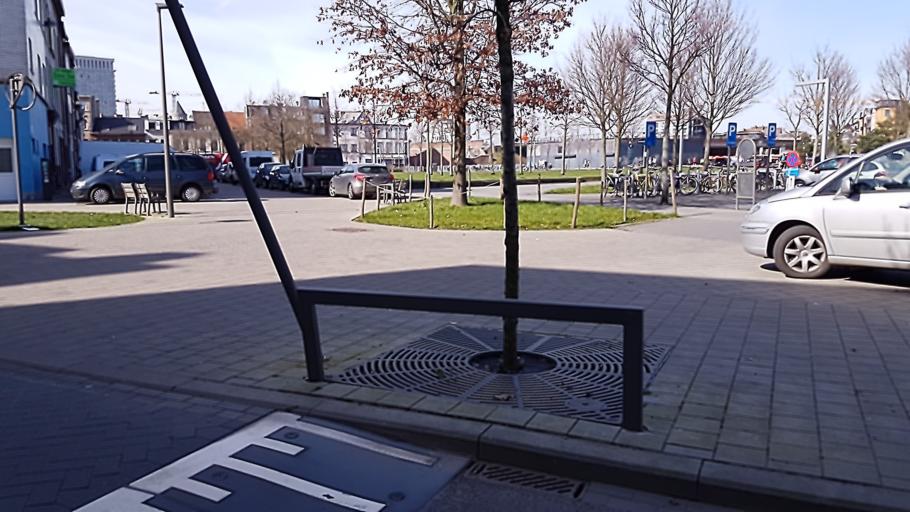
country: BE
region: Flanders
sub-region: Provincie Antwerpen
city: Antwerpen
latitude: 51.2287
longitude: 4.4261
